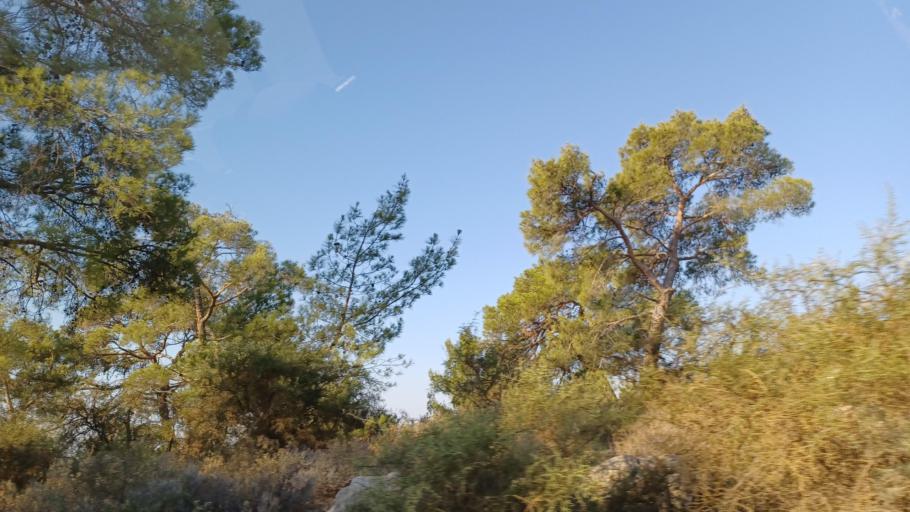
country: CY
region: Limassol
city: Pissouri
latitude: 34.7269
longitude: 32.6799
